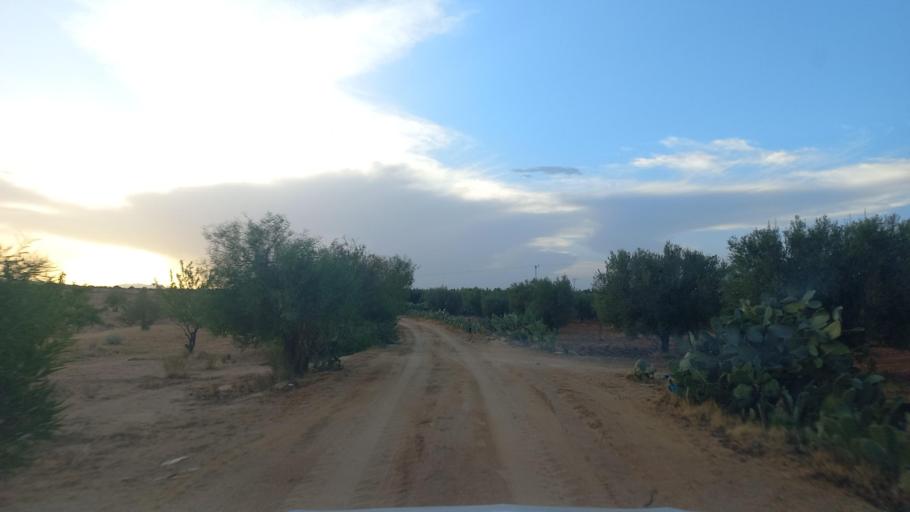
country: TN
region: Al Qasrayn
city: Kasserine
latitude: 35.2118
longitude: 9.0479
